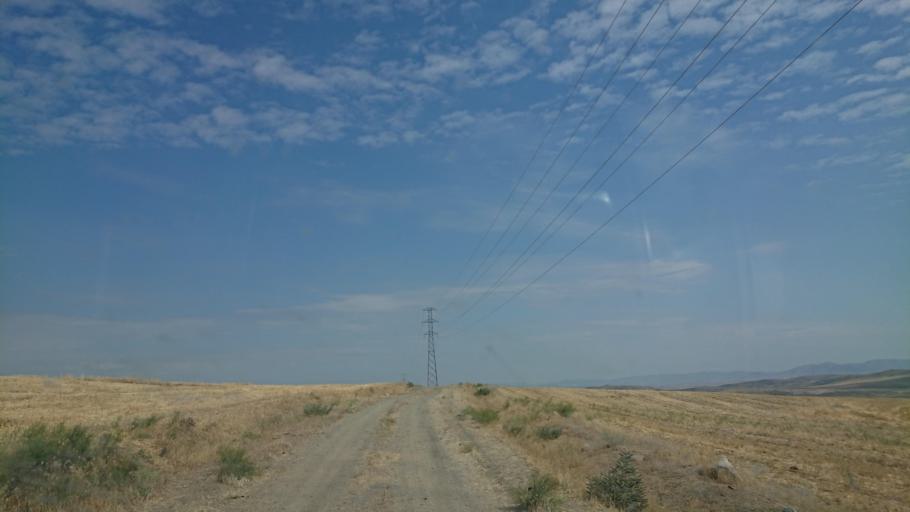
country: TR
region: Aksaray
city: Agacoren
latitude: 38.9496
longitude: 33.9121
